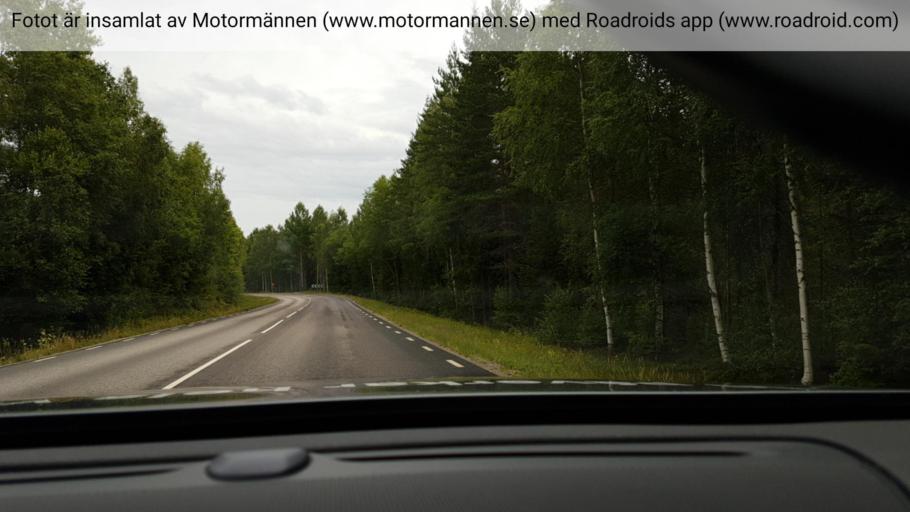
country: SE
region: Dalarna
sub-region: Ludvika Kommun
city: Ludvika
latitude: 60.2906
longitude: 15.2526
